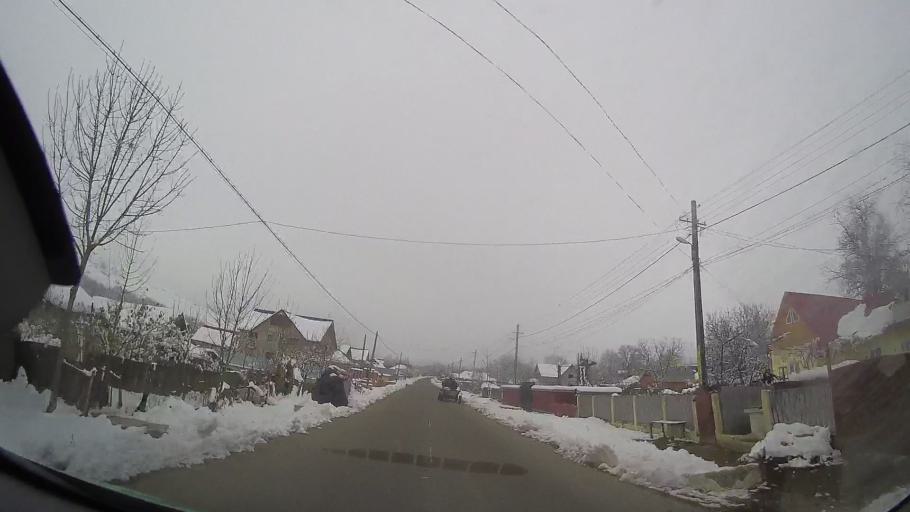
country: RO
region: Neamt
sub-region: Comuna Bozieni
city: Bozieni
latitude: 46.8359
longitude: 27.1575
